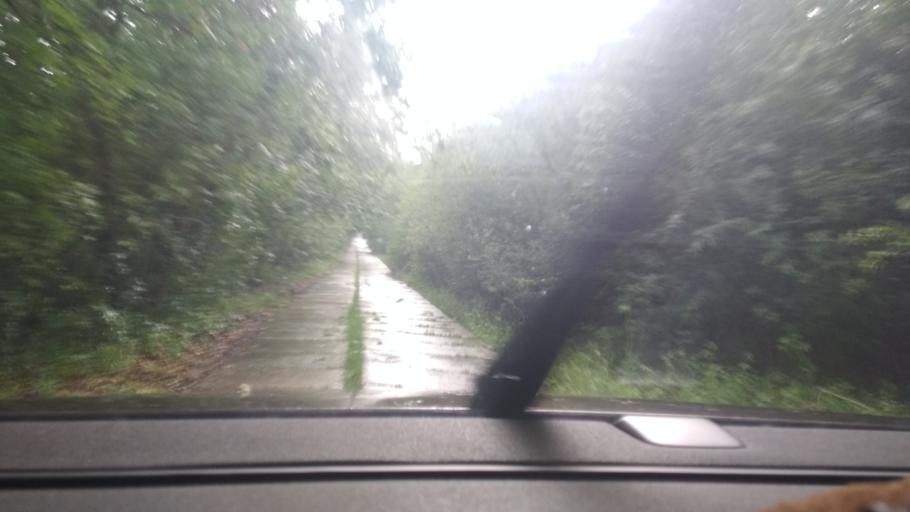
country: MD
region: Singerei
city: Biruinta
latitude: 47.7511
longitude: 28.1443
